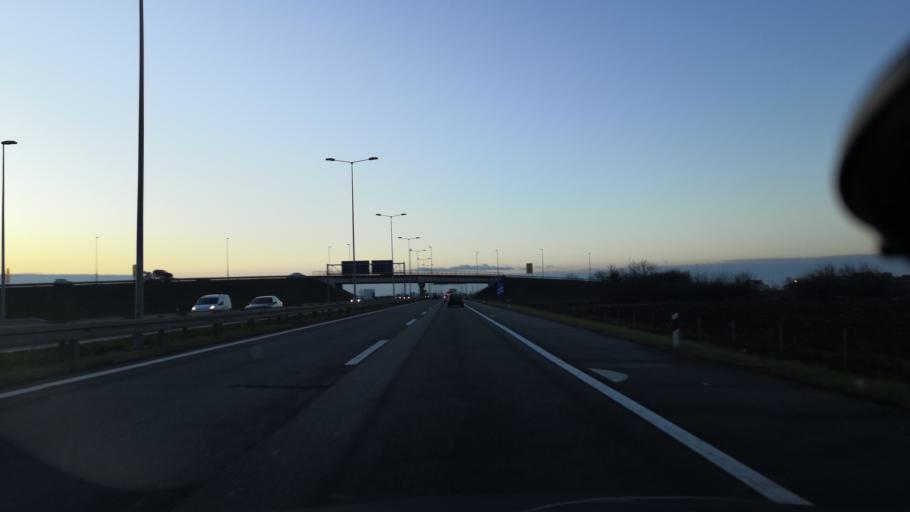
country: RS
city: Dobanovci
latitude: 44.8438
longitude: 20.2138
